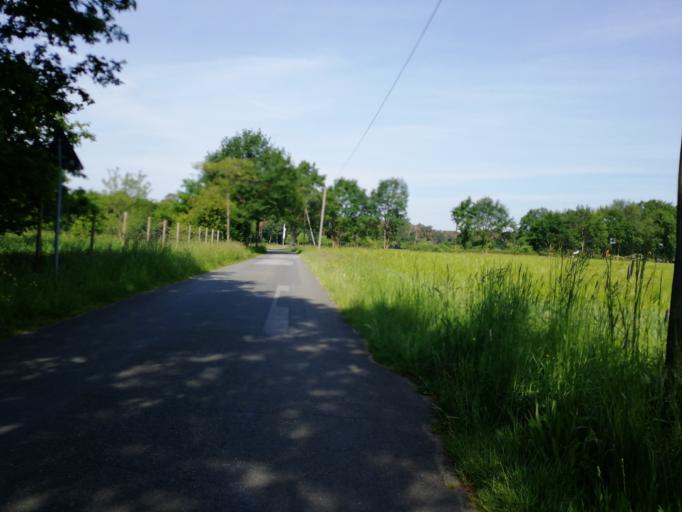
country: DE
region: North Rhine-Westphalia
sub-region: Regierungsbezirk Detmold
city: Verl
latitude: 51.9035
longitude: 8.5077
